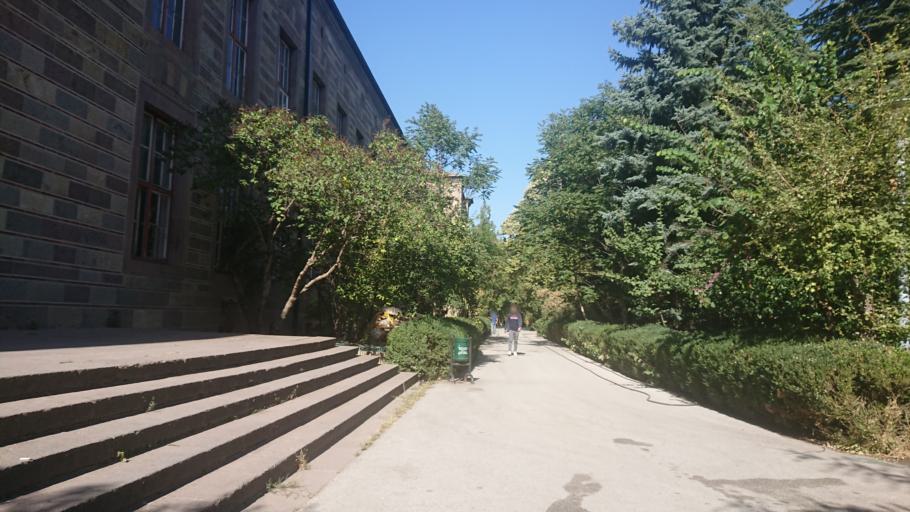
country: TR
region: Ankara
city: Ankara
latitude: 39.9348
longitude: 32.8315
